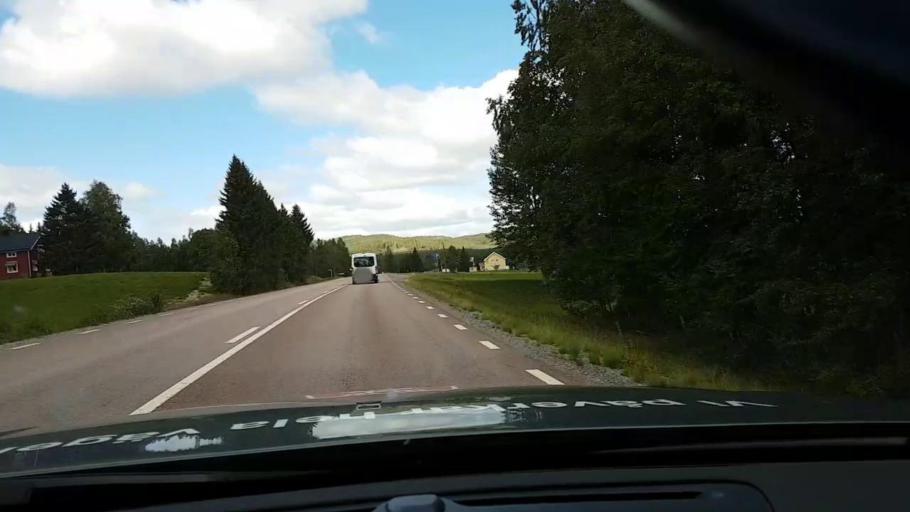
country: SE
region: Vaesternorrland
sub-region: OErnskoeldsviks Kommun
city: Bjasta
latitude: 63.3690
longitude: 18.4418
